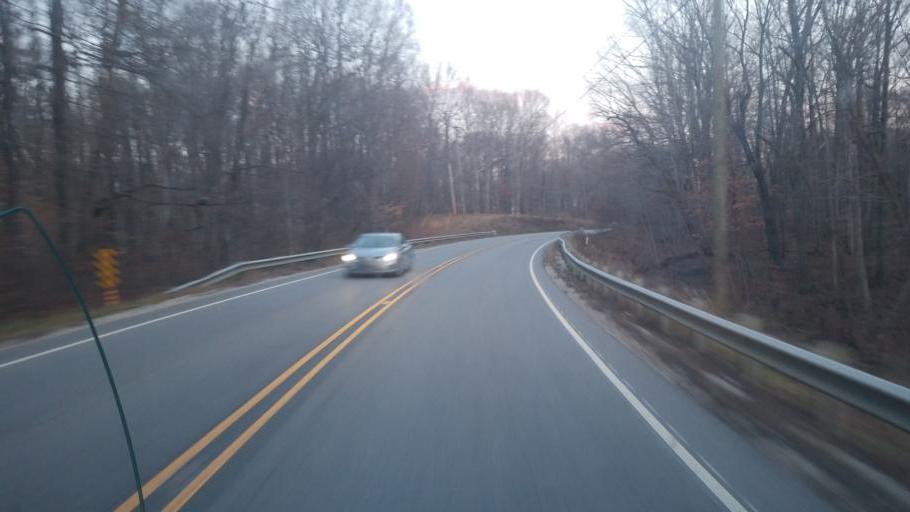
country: US
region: Indiana
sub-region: Lawrence County
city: Bedford
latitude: 38.8746
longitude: -86.3007
